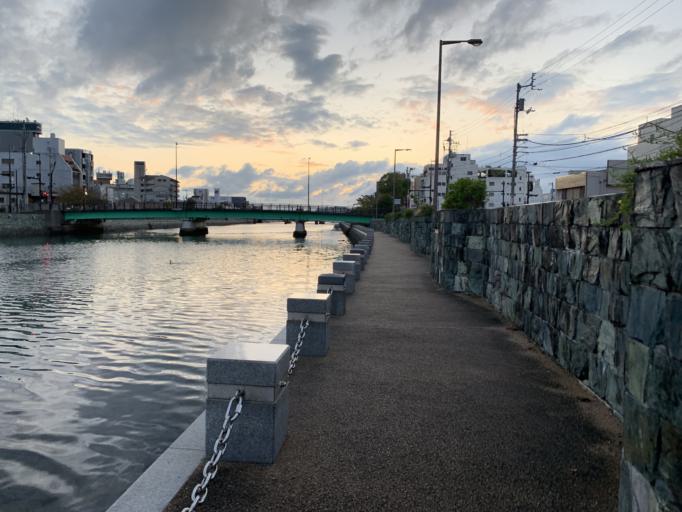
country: JP
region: Tokushima
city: Tokushima-shi
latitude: 34.0675
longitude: 134.5528
